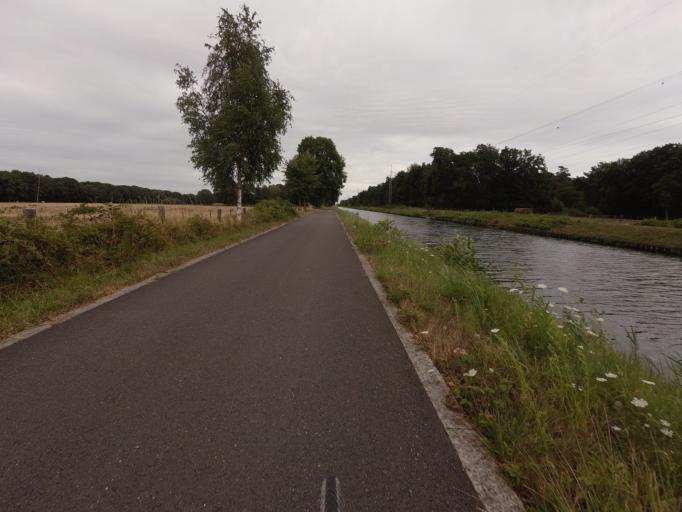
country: BE
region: Flanders
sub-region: Provincie Antwerpen
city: Brecht
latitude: 51.3204
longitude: 4.6143
